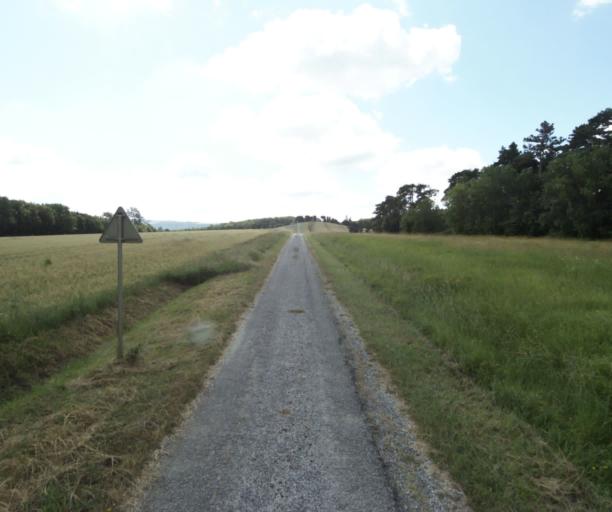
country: FR
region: Midi-Pyrenees
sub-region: Departement de la Haute-Garonne
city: Saint-Felix-Lauragais
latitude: 43.4302
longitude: 1.9270
